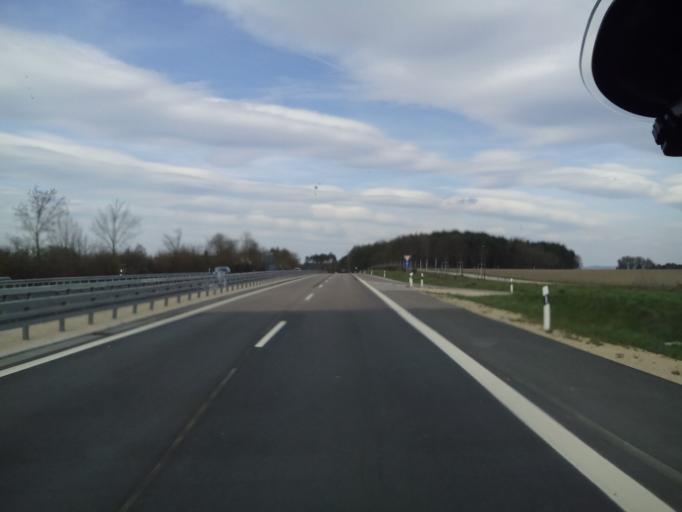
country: DE
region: Bavaria
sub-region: Regierungsbezirk Mittelfranken
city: Roth
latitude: 49.2205
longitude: 11.0850
